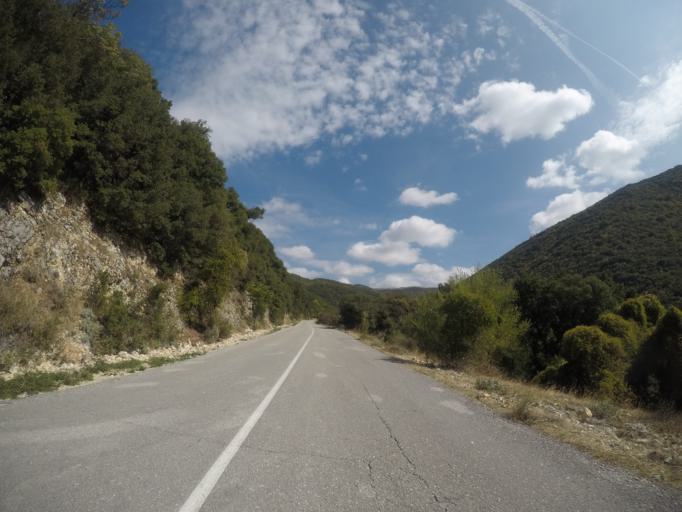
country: GR
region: Epirus
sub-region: Nomos Ioanninon
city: Kalpaki
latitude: 39.9035
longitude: 20.6546
